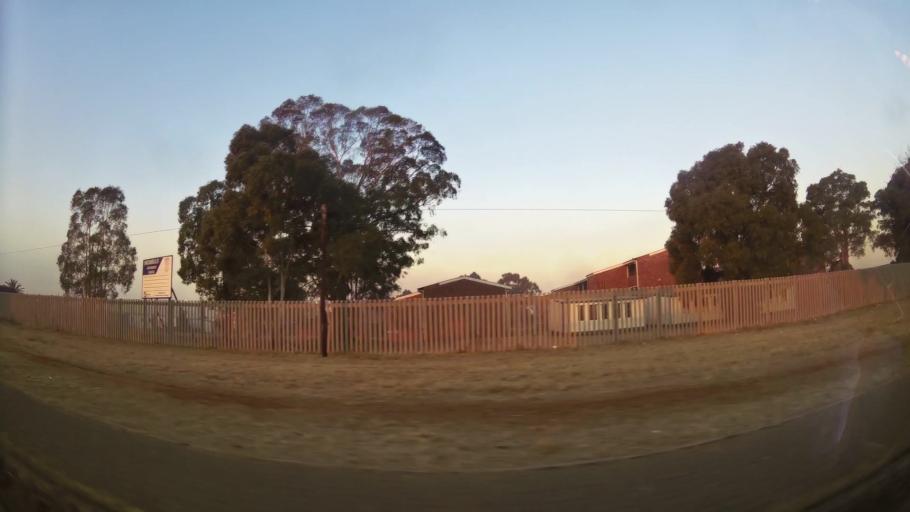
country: ZA
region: Gauteng
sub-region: Ekurhuleni Metropolitan Municipality
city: Springs
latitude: -26.2938
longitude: 28.4072
